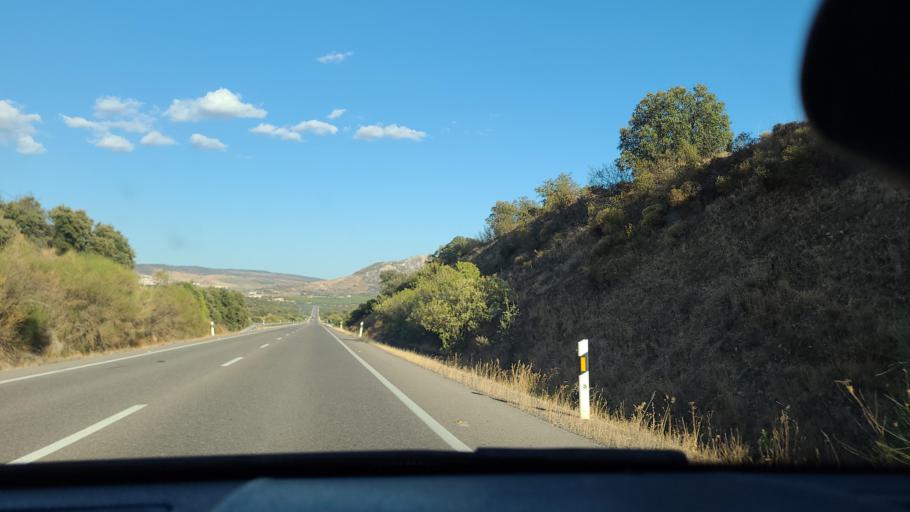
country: ES
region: Andalusia
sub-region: Province of Cordoba
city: Espiel
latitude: 38.1898
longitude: -5.0865
